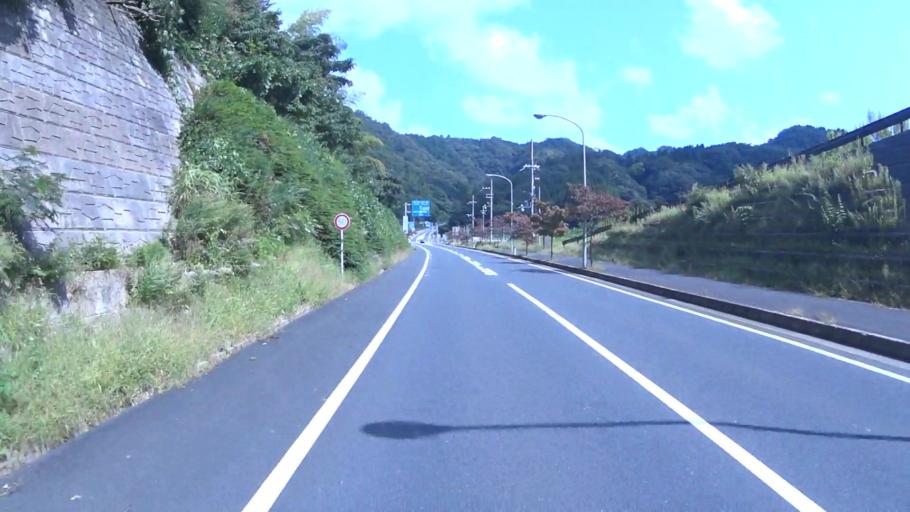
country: JP
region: Kyoto
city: Miyazu
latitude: 35.6718
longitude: 135.2712
